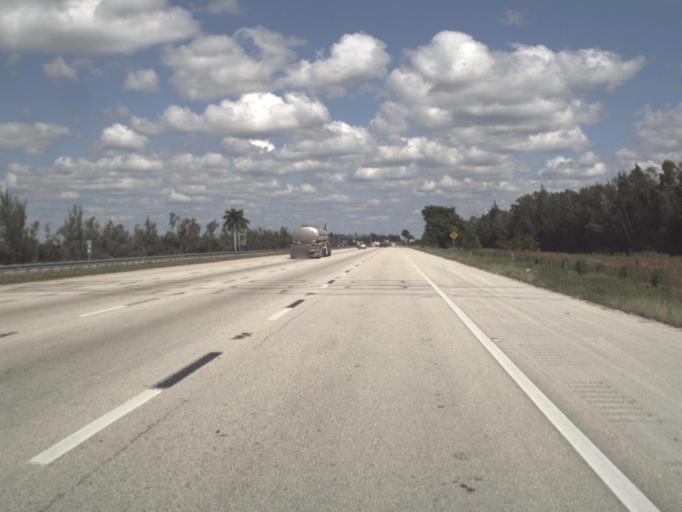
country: US
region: Florida
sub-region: Miami-Dade County
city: Palm Springs North
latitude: 25.9118
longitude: -80.3812
